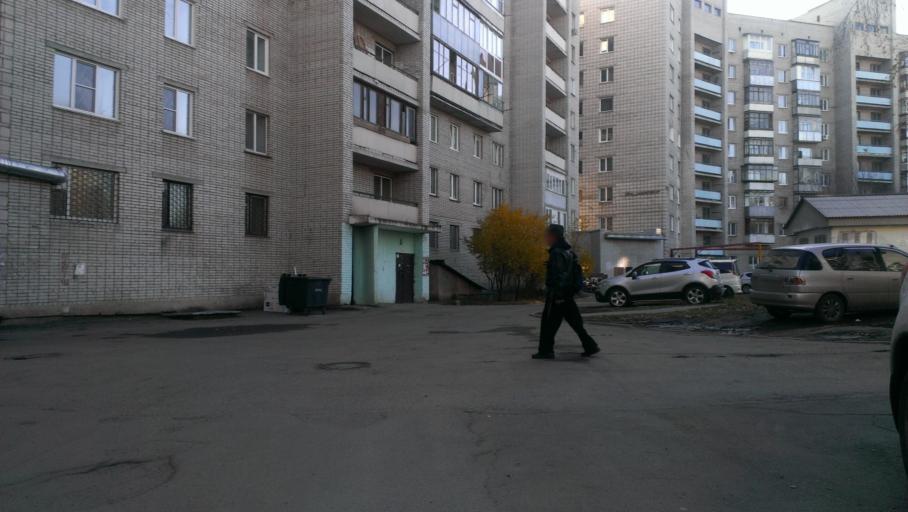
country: RU
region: Altai Krai
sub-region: Gorod Barnaulskiy
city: Barnaul
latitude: 53.3437
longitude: 83.6944
